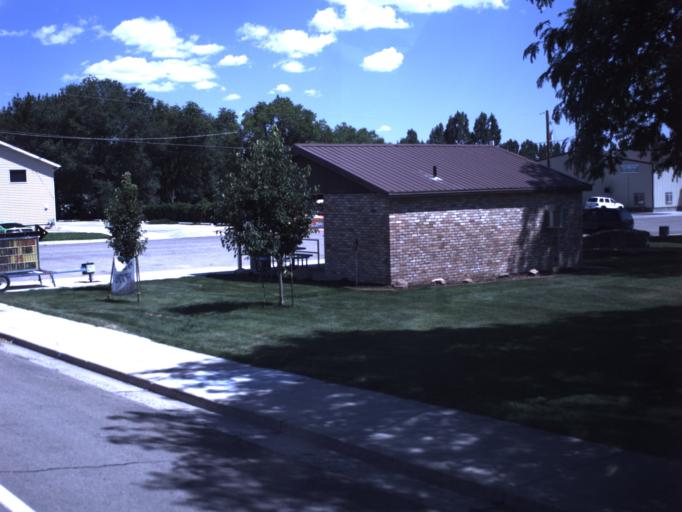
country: US
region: Utah
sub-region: Emery County
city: Castle Dale
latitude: 39.2117
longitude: -111.0127
